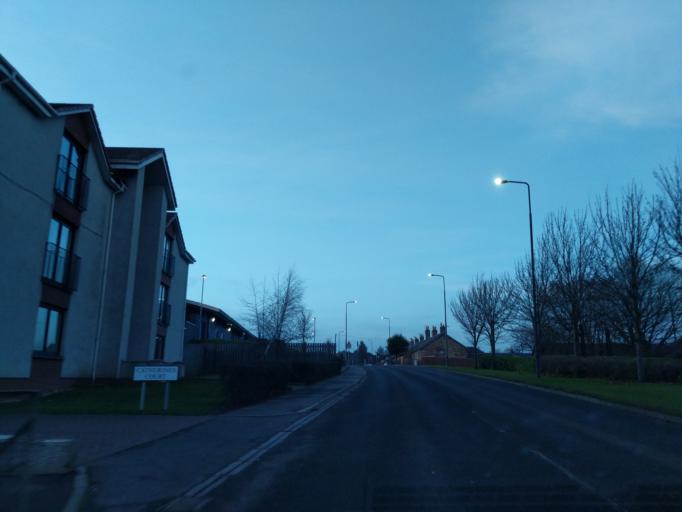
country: GB
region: Scotland
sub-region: Midlothian
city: Bonnyrigg
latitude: 55.8708
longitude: -3.0958
